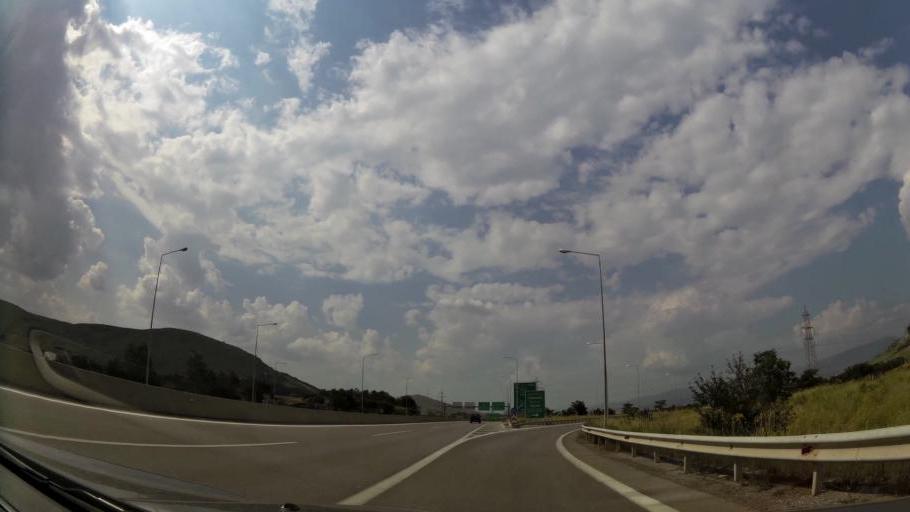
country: GR
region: West Macedonia
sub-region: Nomos Kozanis
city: Koila
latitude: 40.3455
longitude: 21.8060
